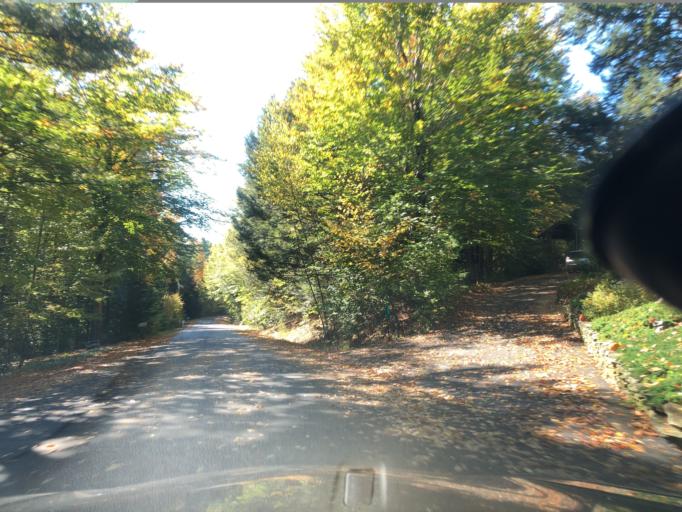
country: US
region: New Hampshire
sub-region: Strafford County
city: Lee
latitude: 43.1235
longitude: -70.9990
